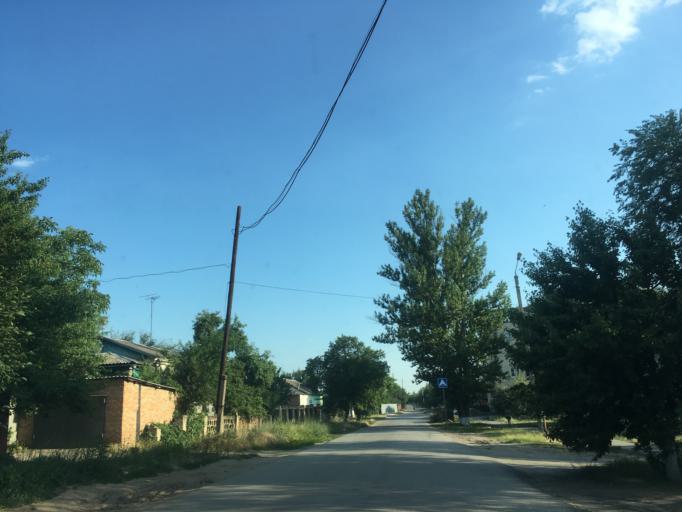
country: RU
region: Rostov
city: Masalovka
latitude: 48.4019
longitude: 40.2775
